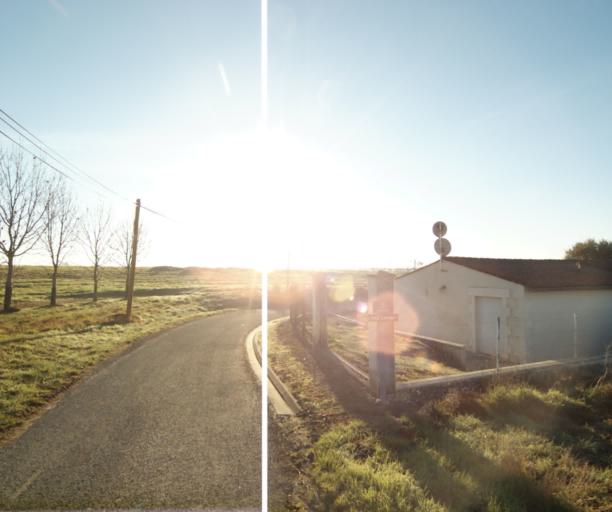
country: FR
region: Poitou-Charentes
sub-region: Departement de la Charente-Maritime
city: Cherac
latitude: 45.6894
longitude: -0.4239
